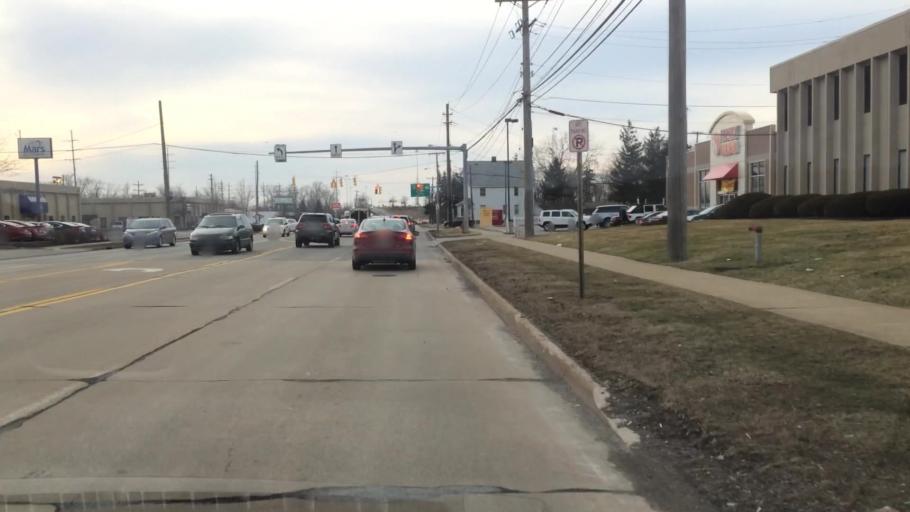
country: US
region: Ohio
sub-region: Cuyahoga County
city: Bedford Heights
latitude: 41.4243
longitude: -81.5156
